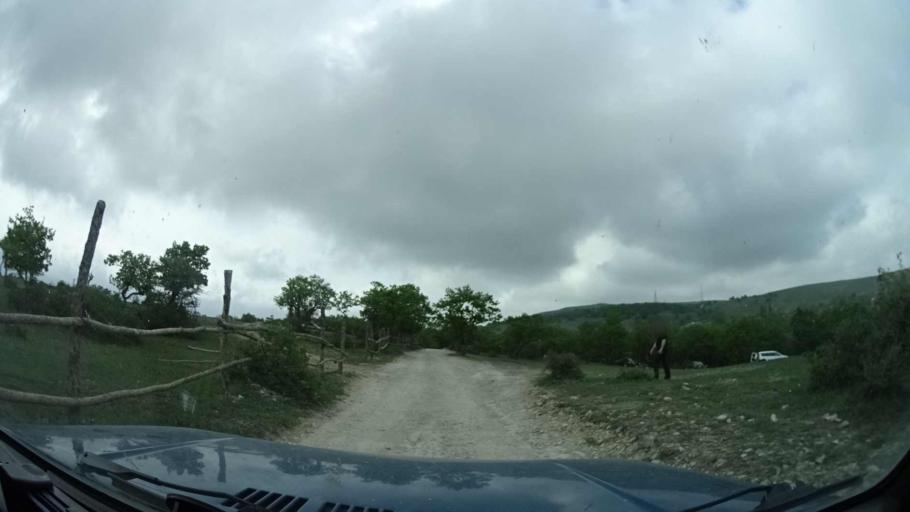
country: RU
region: Dagestan
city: Dubki
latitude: 43.0197
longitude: 46.8321
